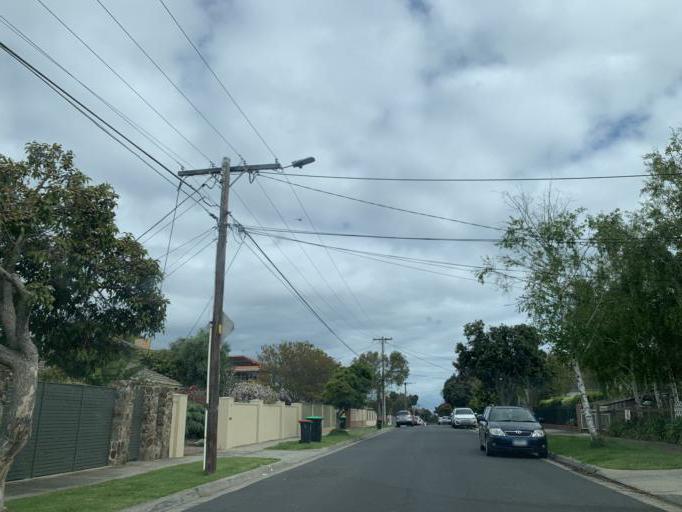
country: AU
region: Victoria
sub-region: Kingston
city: Mentone
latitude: -37.9836
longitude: 145.0551
